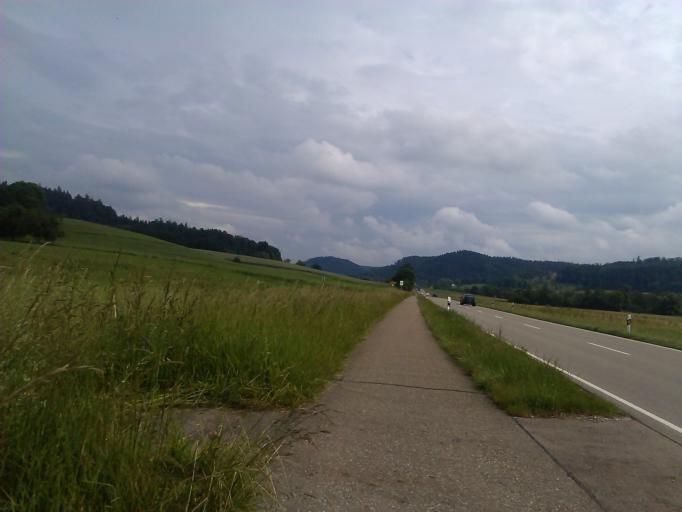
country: DE
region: Baden-Wuerttemberg
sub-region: Regierungsbezirk Stuttgart
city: Gaildorf
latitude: 48.9870
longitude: 9.7506
